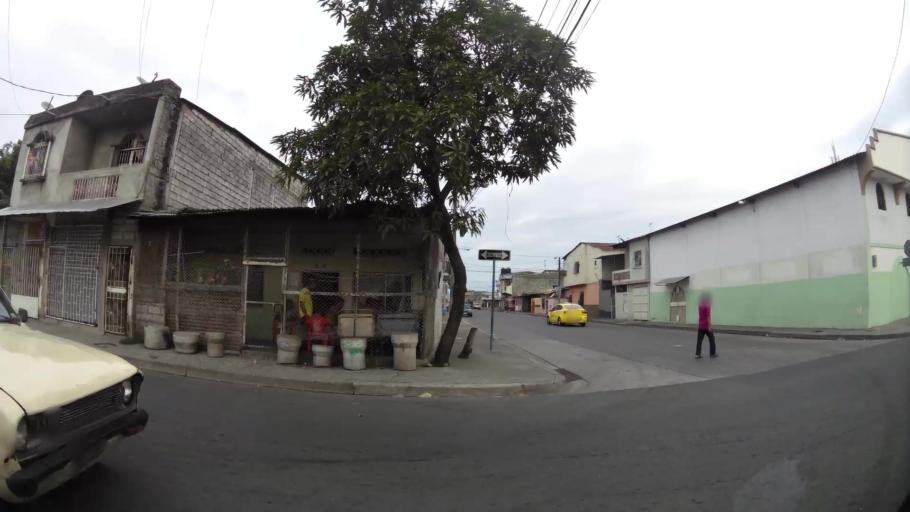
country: EC
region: Guayas
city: Guayaquil
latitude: -2.2683
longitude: -79.8874
